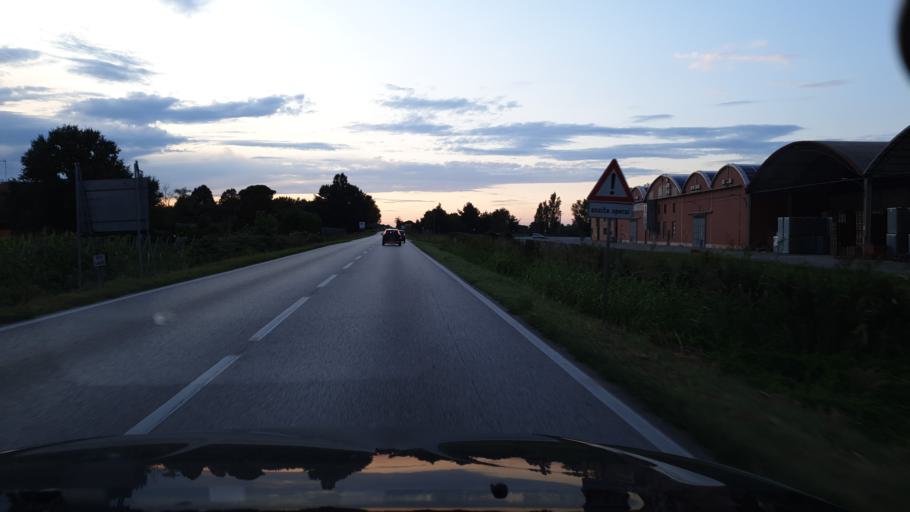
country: IT
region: Emilia-Romagna
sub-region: Provincia di Ravenna
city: Fornace Zarattini
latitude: 44.4325
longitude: 12.1489
